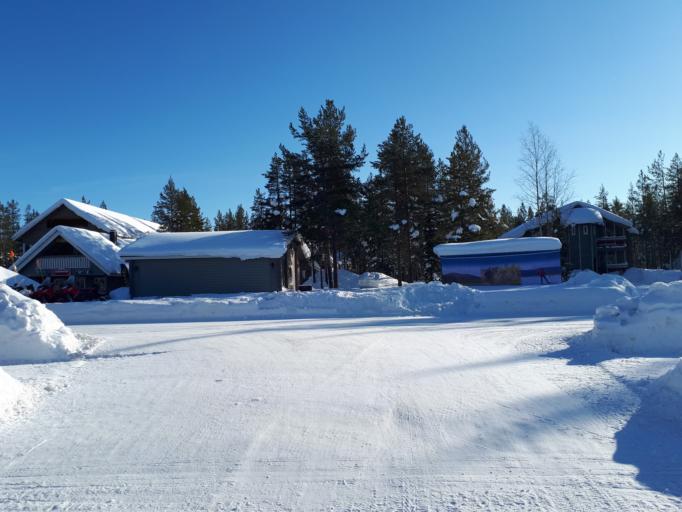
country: FI
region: Lapland
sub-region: Tunturi-Lappi
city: Kolari
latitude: 67.6004
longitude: 24.1529
